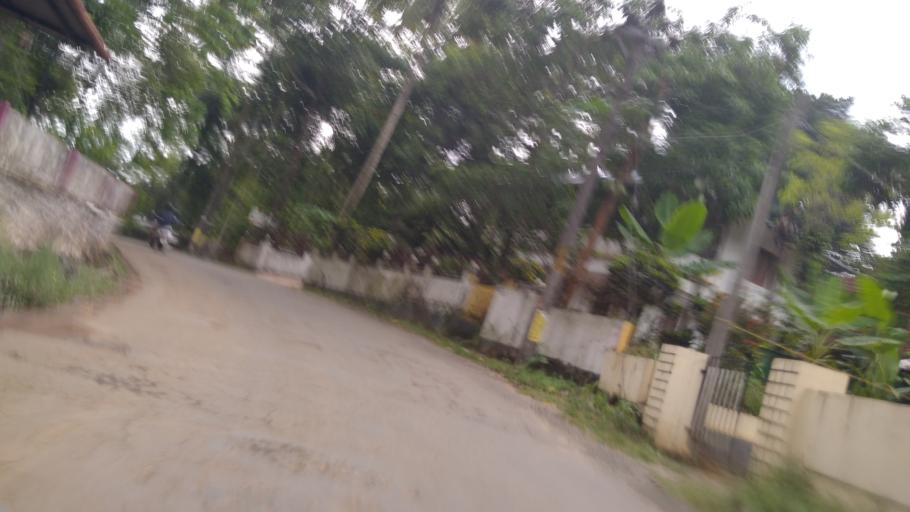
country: IN
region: Kerala
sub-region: Ernakulam
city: Perumpavur
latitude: 10.1208
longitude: 76.5545
